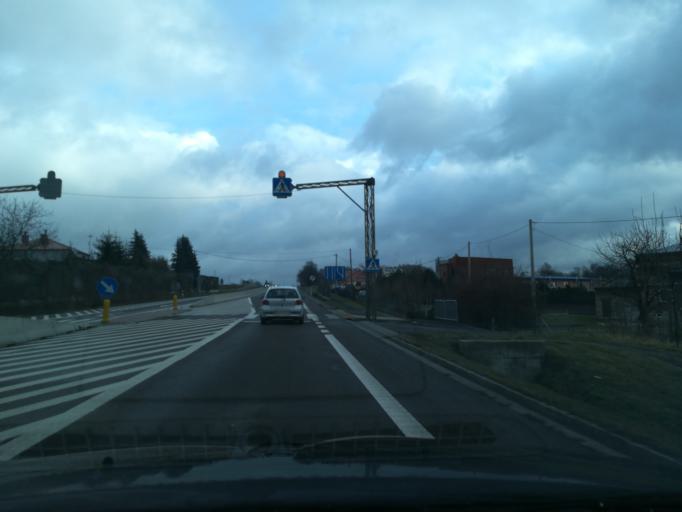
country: PL
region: Subcarpathian Voivodeship
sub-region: Powiat lancucki
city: Kraczkowa
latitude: 50.0472
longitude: 22.1644
